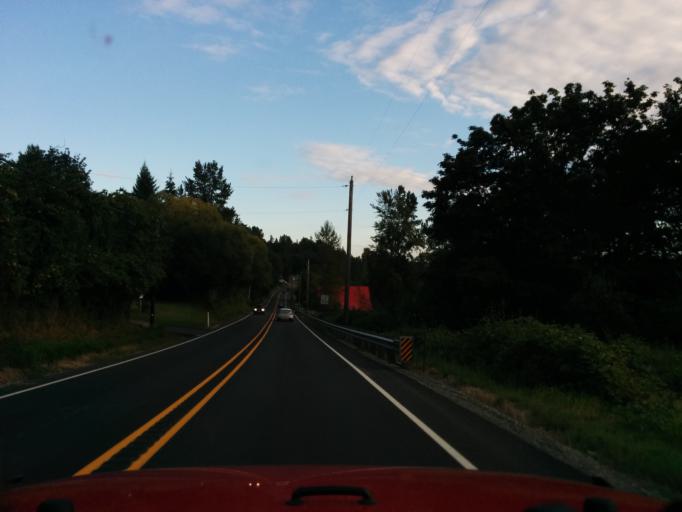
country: US
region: Washington
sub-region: King County
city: Duvall
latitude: 47.7243
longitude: -121.9867
